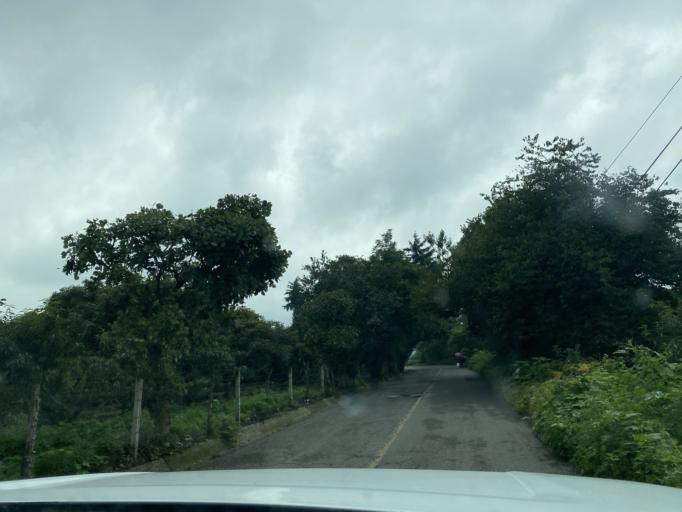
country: MX
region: Morelos
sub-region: Yecapixtla
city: Texcala
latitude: 18.9337
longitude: -98.8079
